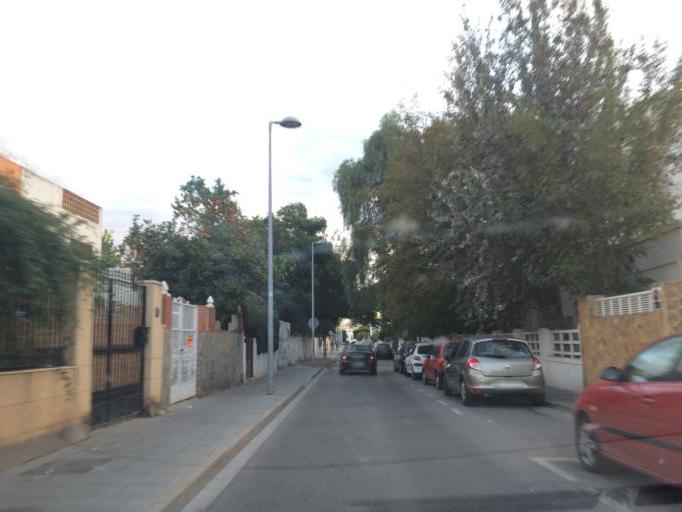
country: ES
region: Andalusia
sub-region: Provincia de Almeria
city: Almeria
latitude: 36.8331
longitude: -2.4511
